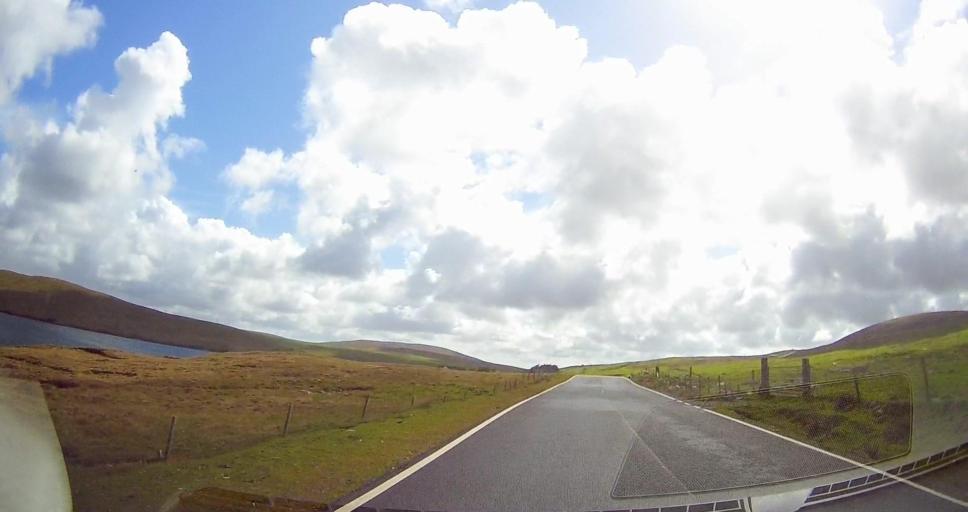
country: GB
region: Scotland
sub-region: Shetland Islands
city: Lerwick
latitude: 60.5398
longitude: -1.3536
